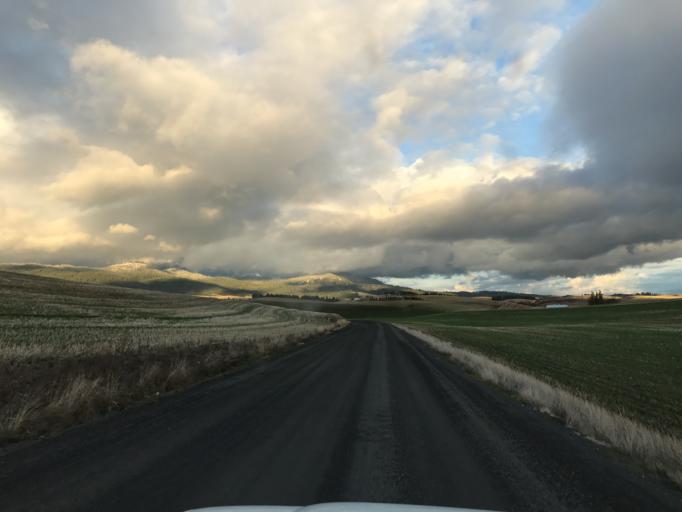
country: US
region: Idaho
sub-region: Latah County
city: Moscow
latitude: 46.7683
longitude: -116.9820
